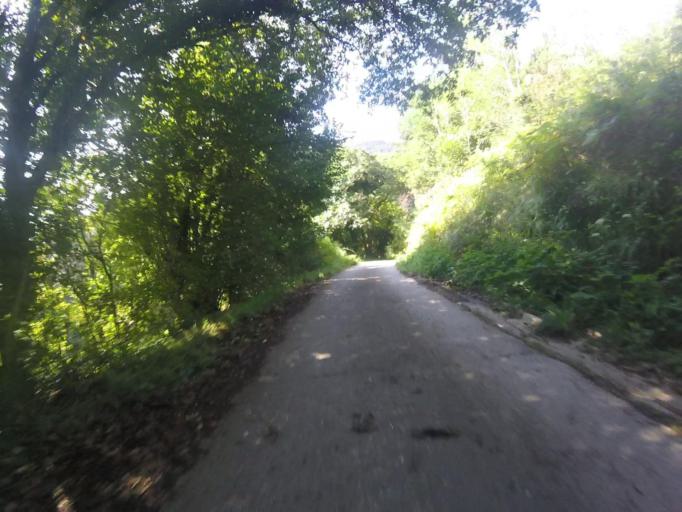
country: ES
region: Basque Country
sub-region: Provincia de Guipuzcoa
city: Irun
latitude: 43.3219
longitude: -1.7443
